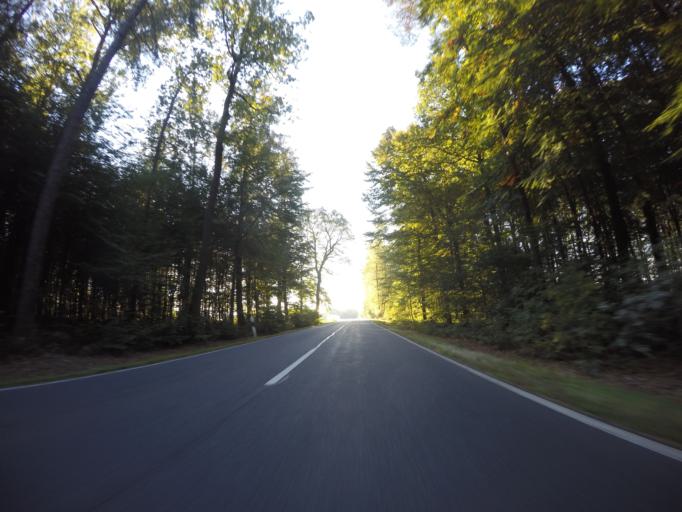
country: DE
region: Bavaria
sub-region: Regierungsbezirk Unterfranken
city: Schollbrunn
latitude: 49.8422
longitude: 9.4519
